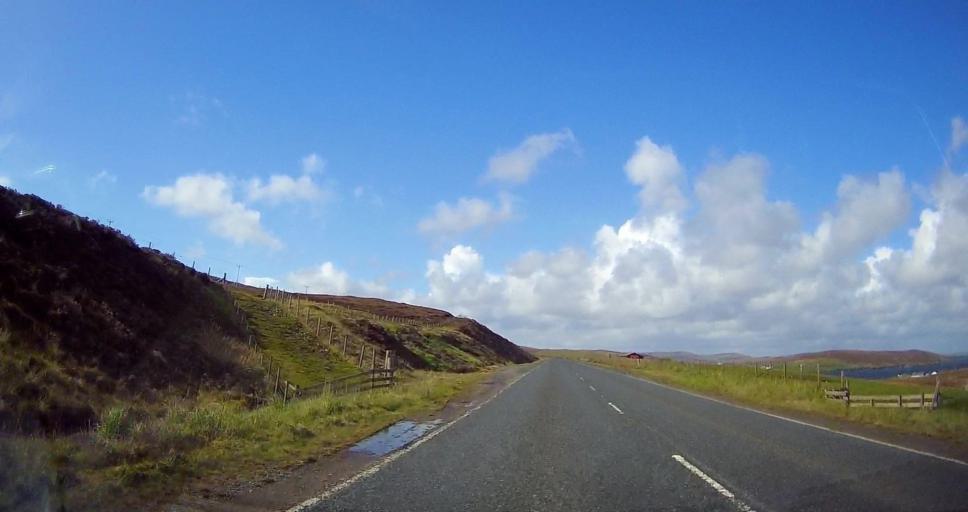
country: GB
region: Scotland
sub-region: Shetland Islands
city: Lerwick
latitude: 60.2196
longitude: -1.2341
